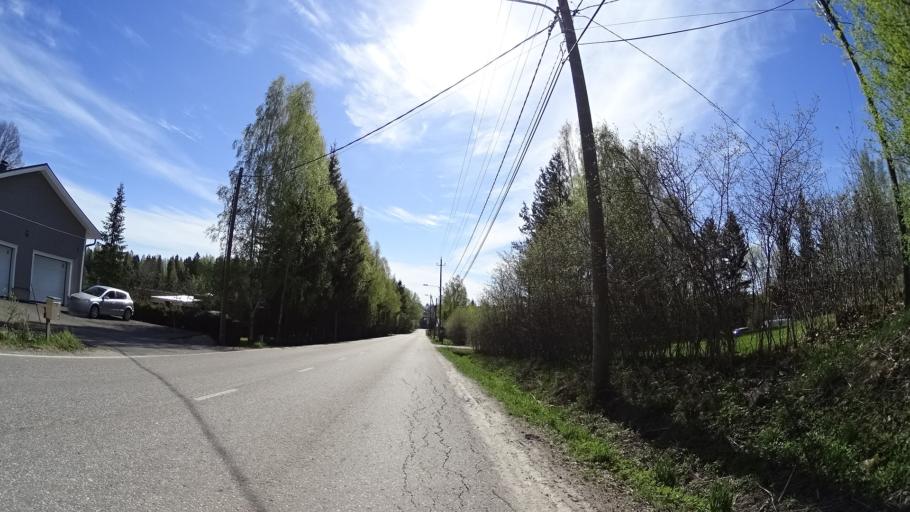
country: FI
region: Uusimaa
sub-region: Helsinki
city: Nurmijaervi
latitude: 60.3685
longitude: 24.8415
